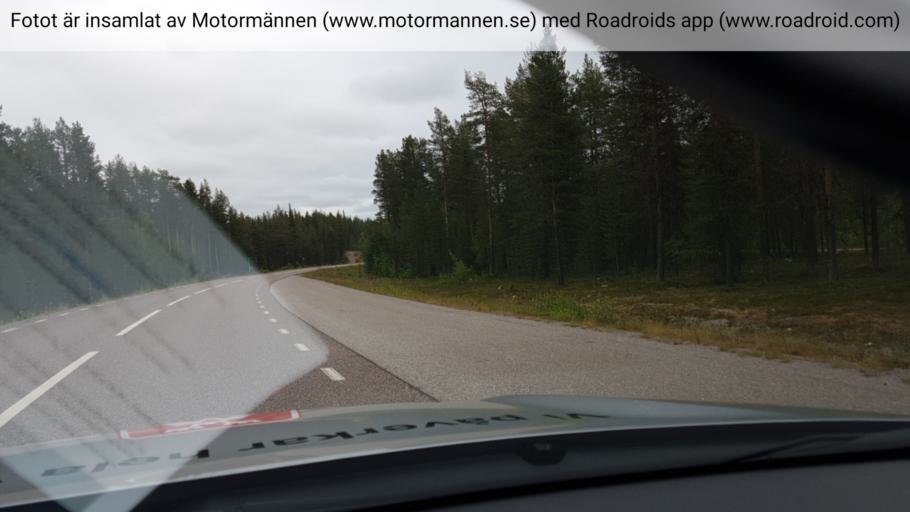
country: SE
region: Norrbotten
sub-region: Gallivare Kommun
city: Gaellivare
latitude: 67.0774
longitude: 21.3412
